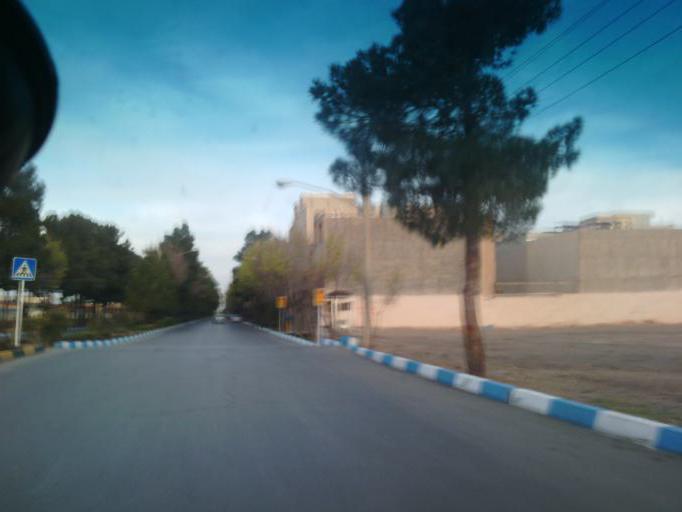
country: IR
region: Isfahan
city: Shahin Shahr
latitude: 32.8753
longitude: 51.5483
